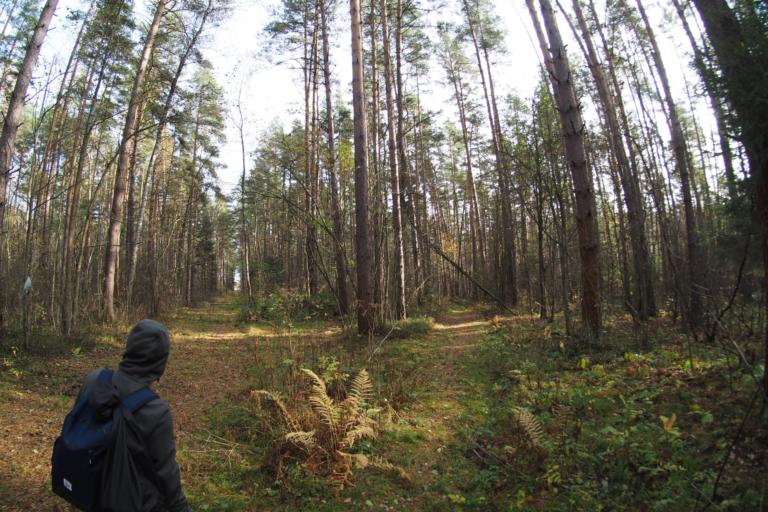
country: RU
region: Moskovskaya
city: Davydovo
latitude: 55.5606
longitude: 38.7978
